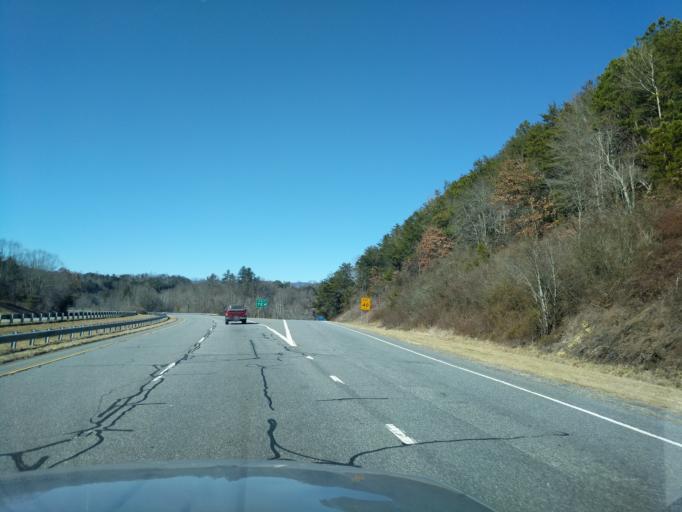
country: US
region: North Carolina
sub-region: Swain County
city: Cherokee
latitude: 35.4294
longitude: -83.3560
